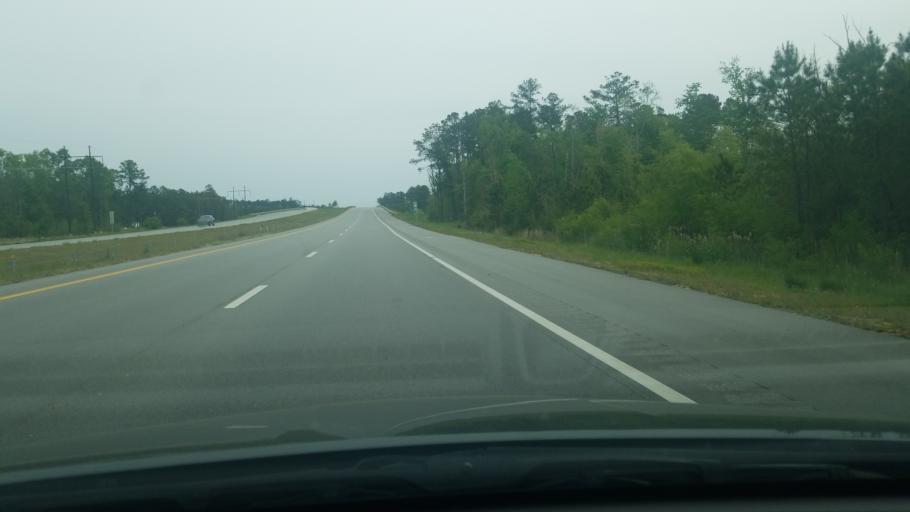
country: US
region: North Carolina
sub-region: Craven County
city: River Bend
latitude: 35.0494
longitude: -77.2152
